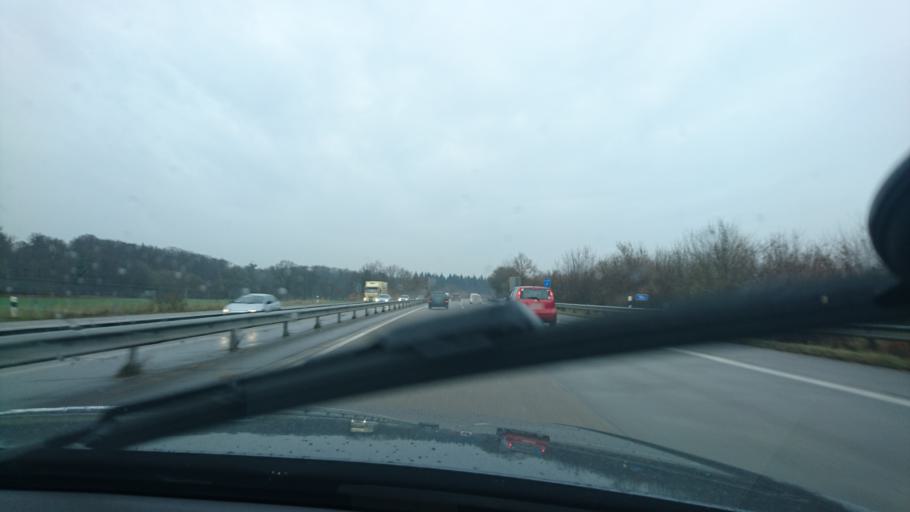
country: DE
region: Schleswig-Holstein
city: Scharbeutz
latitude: 54.0438
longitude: 10.7288
